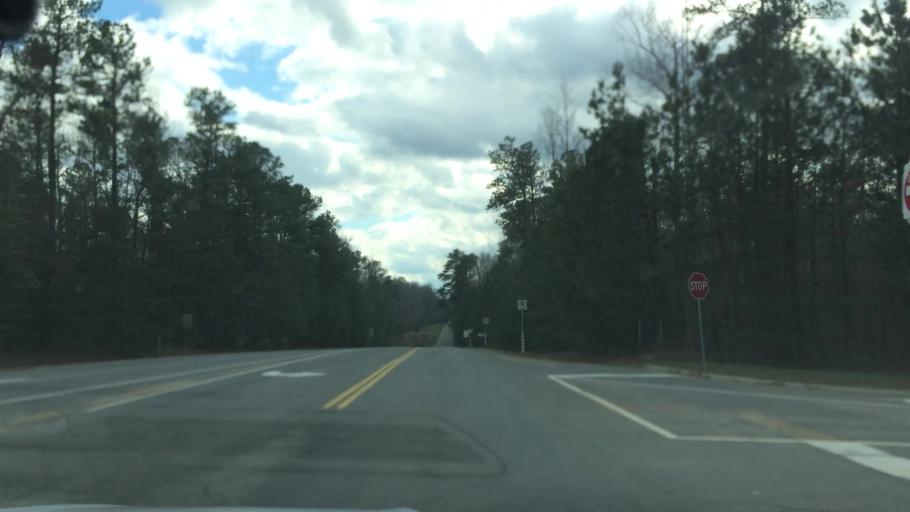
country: US
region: Virginia
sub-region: New Kent County
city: New Kent
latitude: 37.4898
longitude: -77.0265
